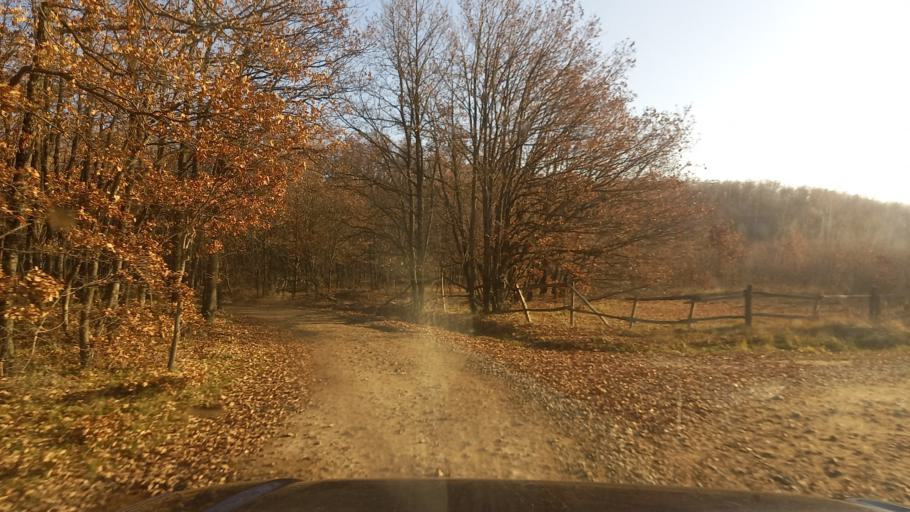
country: RU
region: Krasnodarskiy
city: Azovskaya
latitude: 44.8067
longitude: 38.5903
